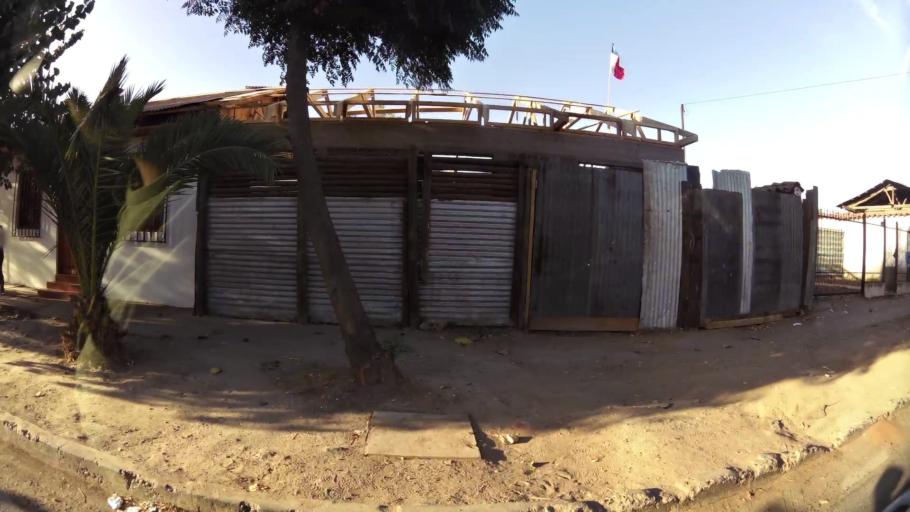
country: CL
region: Maule
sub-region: Provincia de Talca
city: Talca
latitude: -35.4376
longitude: -71.6458
